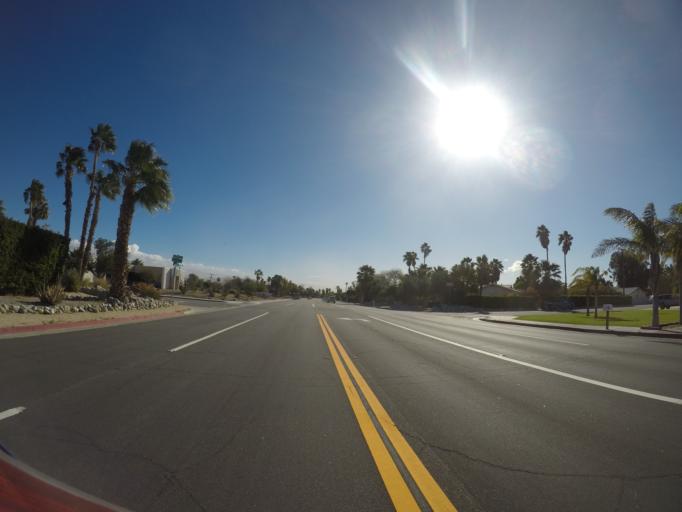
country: US
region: California
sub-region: Riverside County
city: Palm Springs
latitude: 33.8522
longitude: -116.5240
